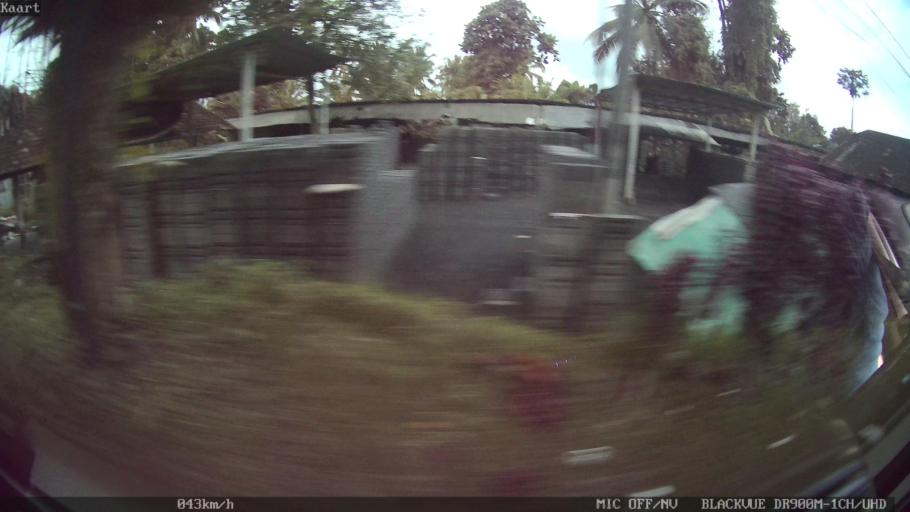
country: ID
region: Bali
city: Pohgending Kangin
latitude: -8.4268
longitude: 115.1445
